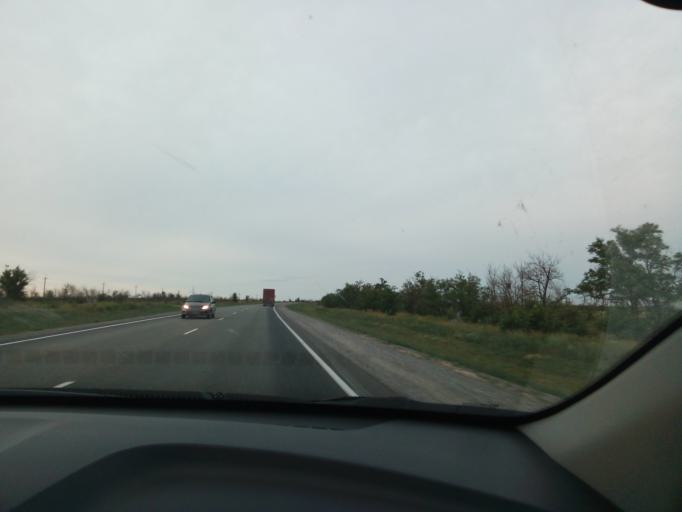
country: RU
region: Volgograd
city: Dubovka
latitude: 49.1454
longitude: 44.8306
